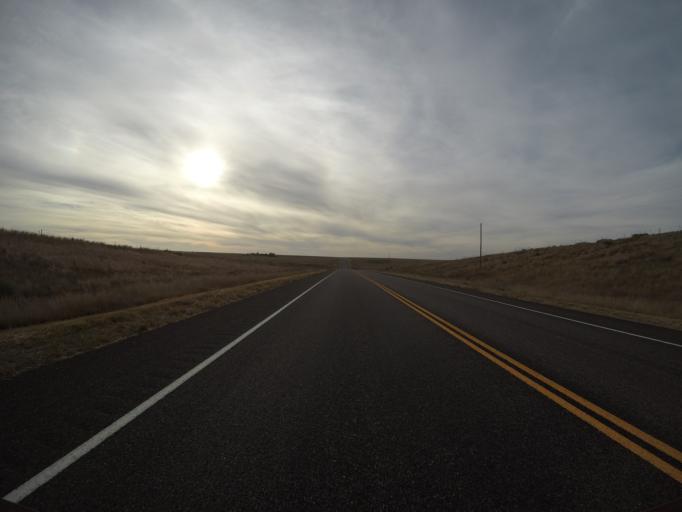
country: US
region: Kansas
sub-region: Cheyenne County
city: Saint Francis
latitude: 39.7467
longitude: -102.0769
